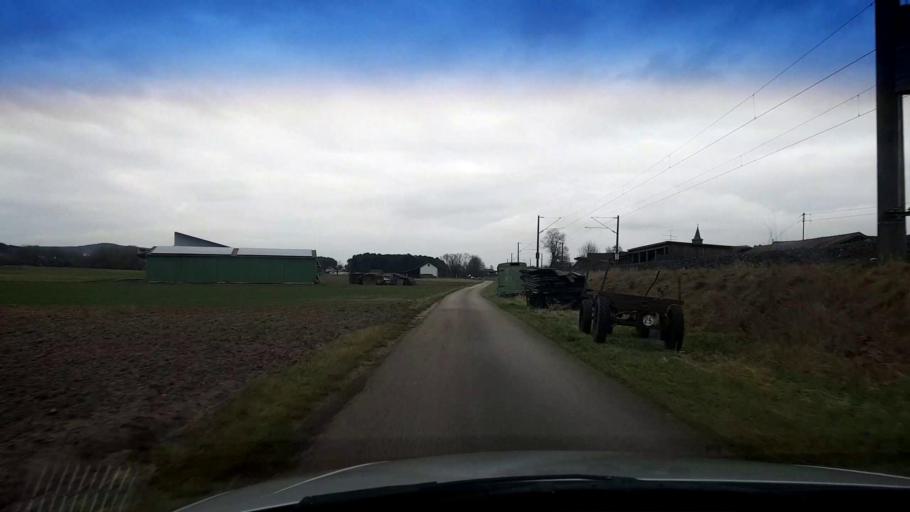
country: DE
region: Bavaria
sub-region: Upper Franconia
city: Viereth-Trunstadt
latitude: 49.9368
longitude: 10.7905
